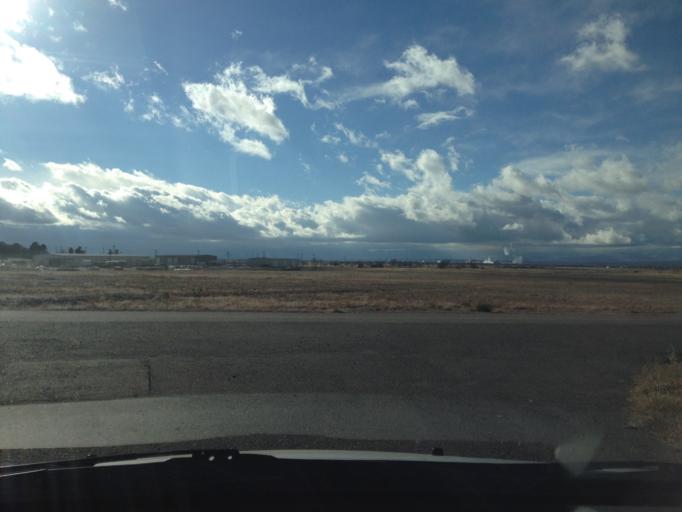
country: US
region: Colorado
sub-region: Adams County
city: Derby
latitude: 39.8329
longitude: -104.8560
